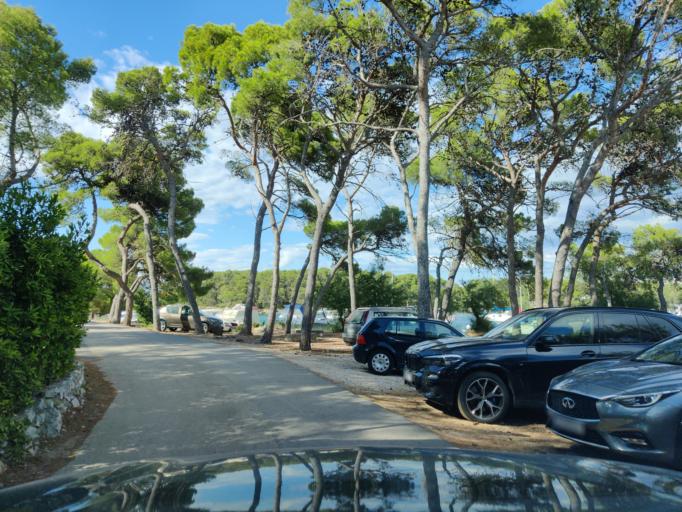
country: HR
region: Sibensko-Kniniska
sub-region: Grad Sibenik
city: Sibenik
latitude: 43.7251
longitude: 15.8474
